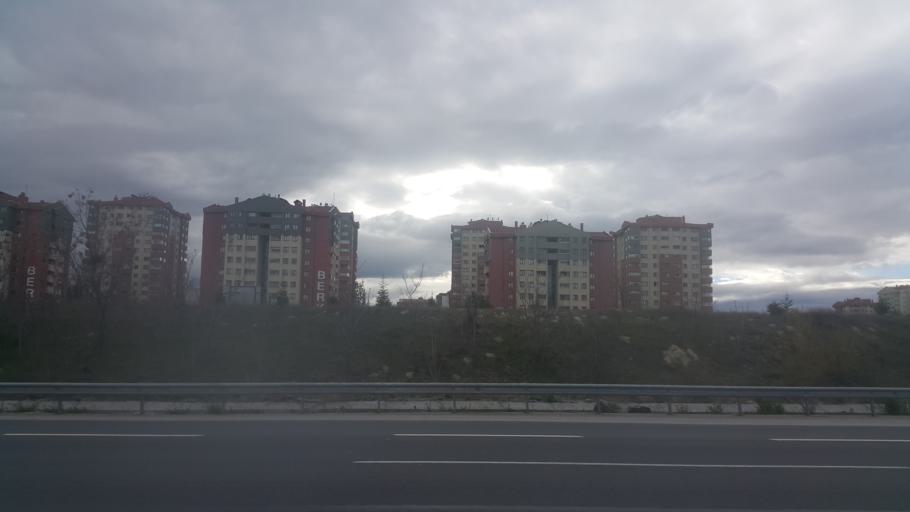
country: TR
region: Ankara
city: Etimesgut
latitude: 39.9897
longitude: 32.6367
